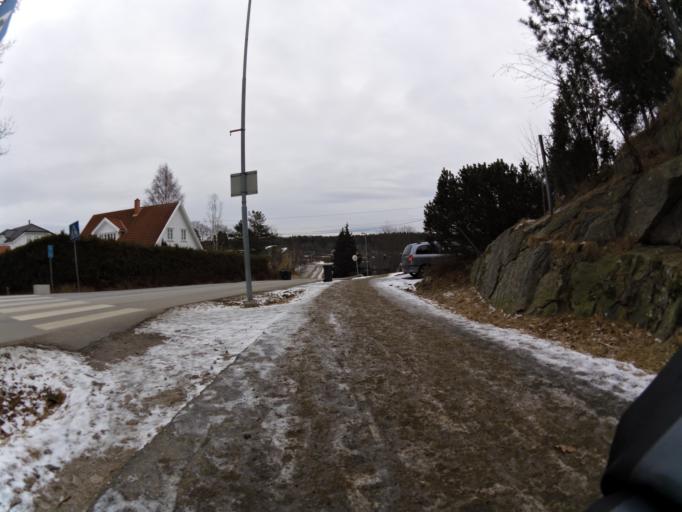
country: NO
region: Ostfold
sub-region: Fredrikstad
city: Fredrikstad
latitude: 59.1994
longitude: 10.8813
